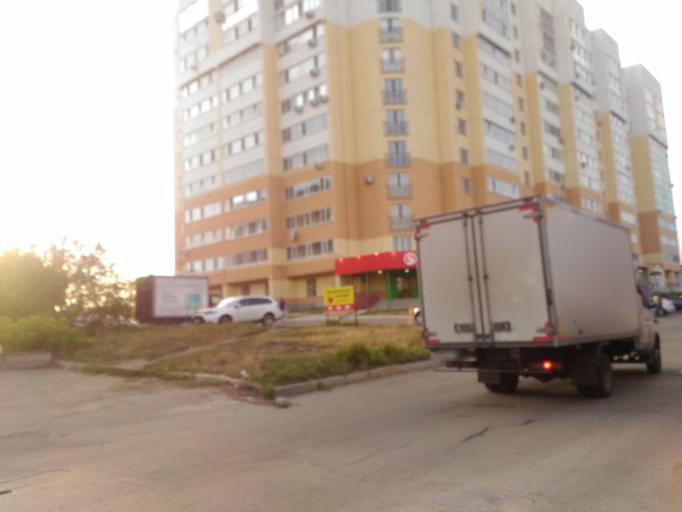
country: RU
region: Ulyanovsk
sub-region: Ulyanovskiy Rayon
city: Ulyanovsk
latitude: 54.3342
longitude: 48.3916
